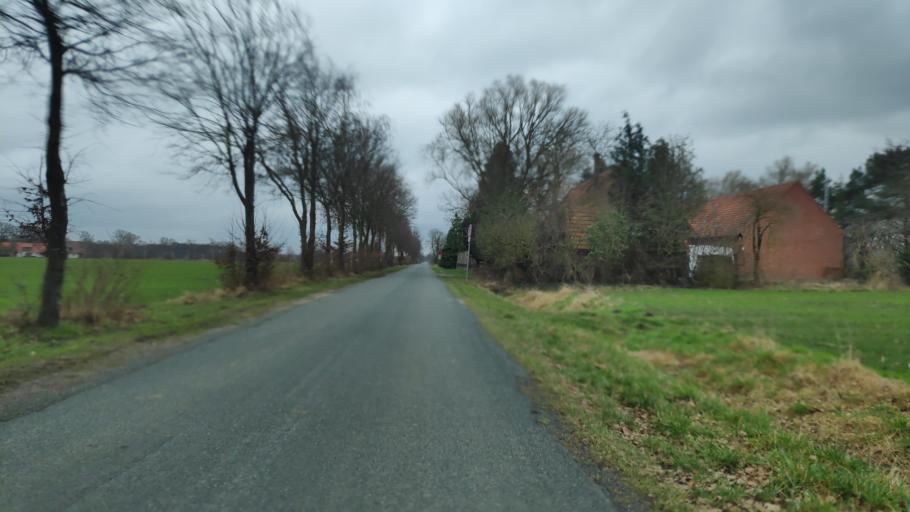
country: DE
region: North Rhine-Westphalia
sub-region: Regierungsbezirk Detmold
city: Hille
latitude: 52.3756
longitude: 8.7731
